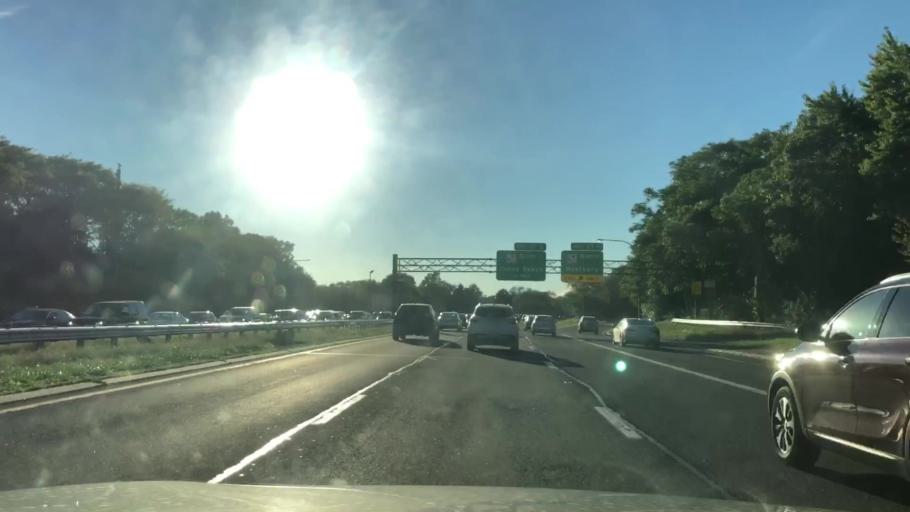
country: US
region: New York
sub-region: Nassau County
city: North Wantagh
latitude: 40.6987
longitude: -73.5140
